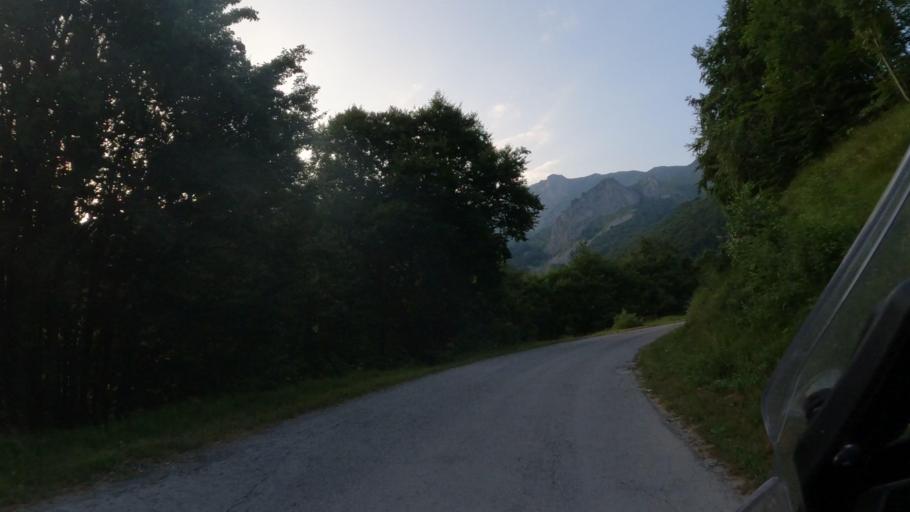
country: IT
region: Piedmont
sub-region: Provincia di Cuneo
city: Limone Piemonte
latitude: 44.1625
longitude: 7.5733
